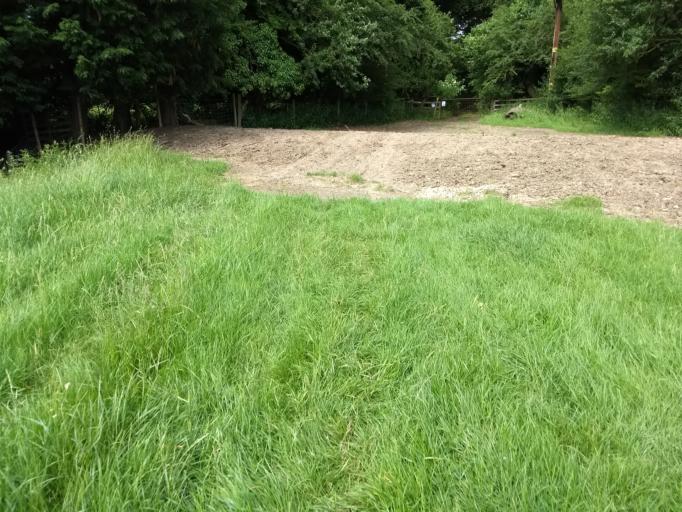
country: GB
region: England
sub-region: Milton Keynes
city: Calverton
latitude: 52.0402
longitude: -0.8504
